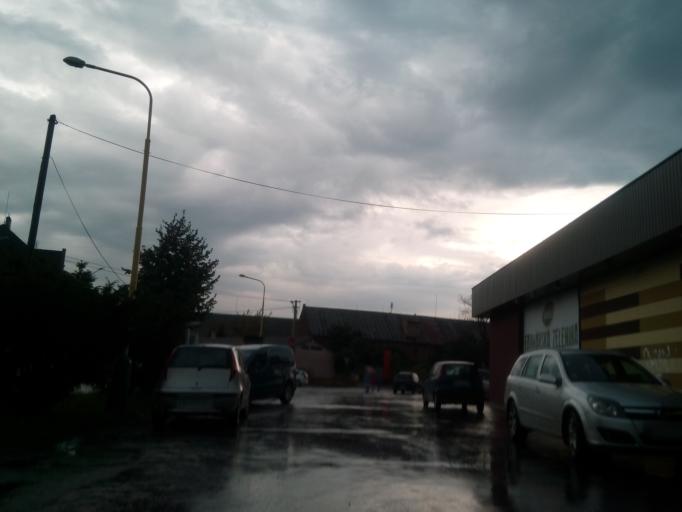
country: SK
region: Kosicky
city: Kosice
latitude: 48.7325
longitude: 21.2603
